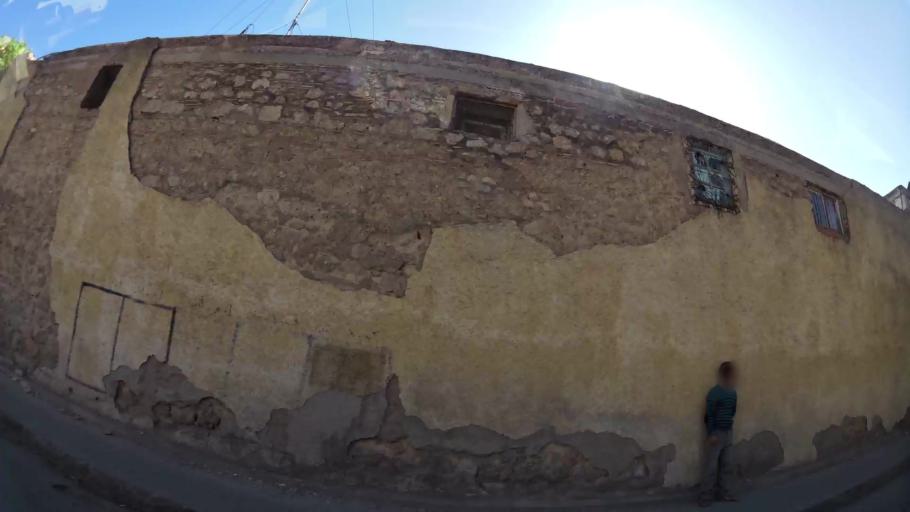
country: MA
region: Fes-Boulemane
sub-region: Fes
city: Fes
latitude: 34.0604
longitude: -4.9644
